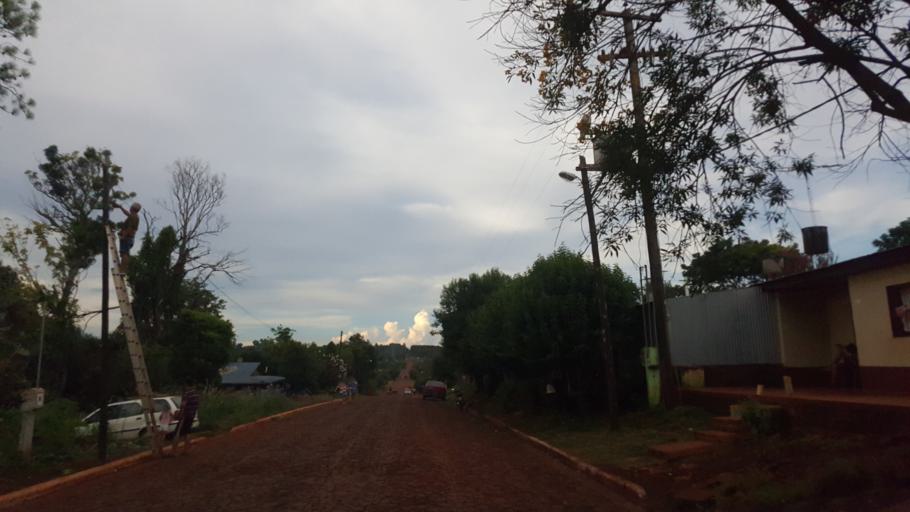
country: AR
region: Misiones
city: Jardin America
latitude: -27.0757
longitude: -55.2864
